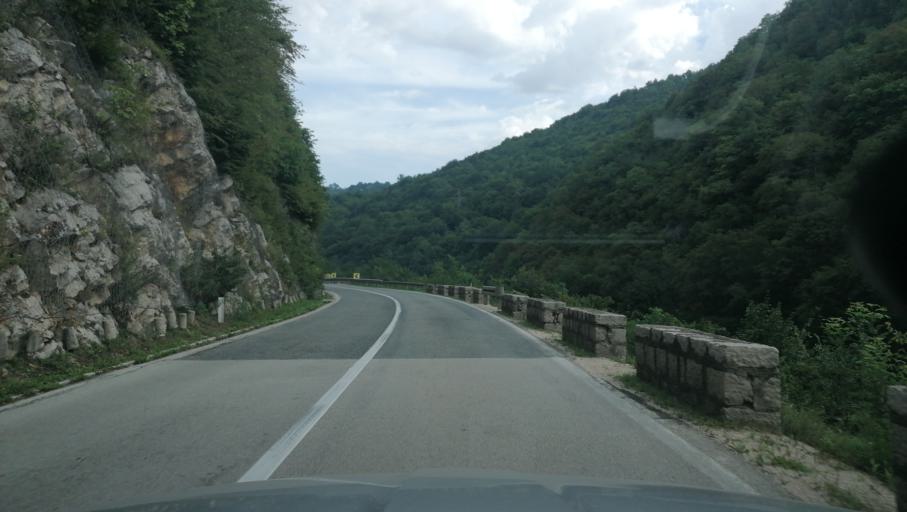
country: BA
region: Republika Srpska
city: Mrkonjic Grad
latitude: 44.5507
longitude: 17.1442
